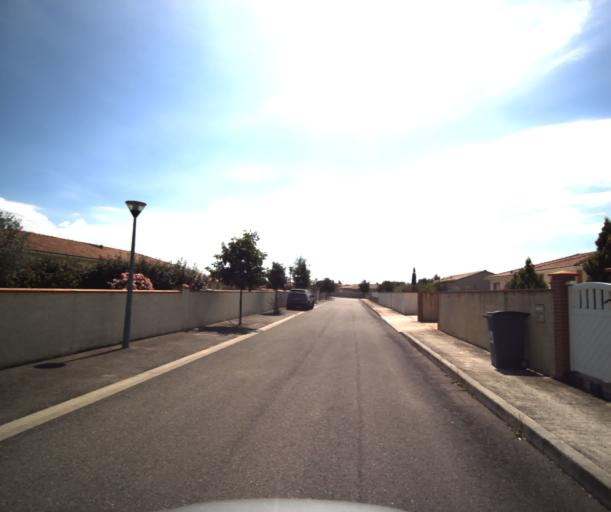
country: FR
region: Midi-Pyrenees
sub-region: Departement de la Haute-Garonne
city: Lacasse
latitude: 43.3911
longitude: 1.2556
